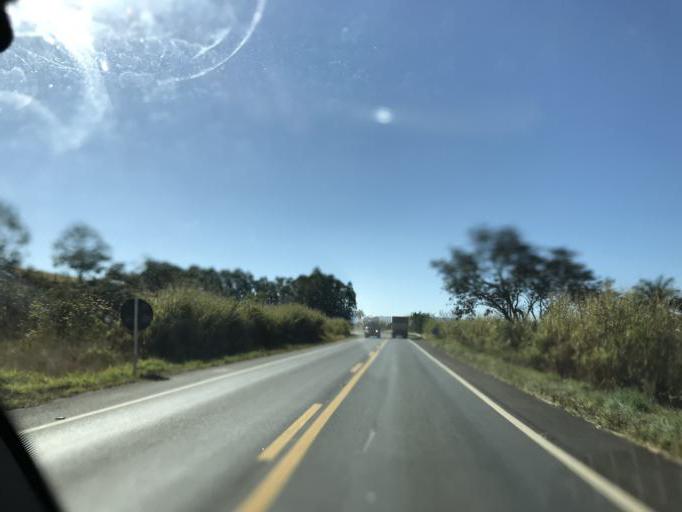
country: BR
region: Minas Gerais
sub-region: Bambui
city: Bambui
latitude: -19.8575
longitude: -45.9865
